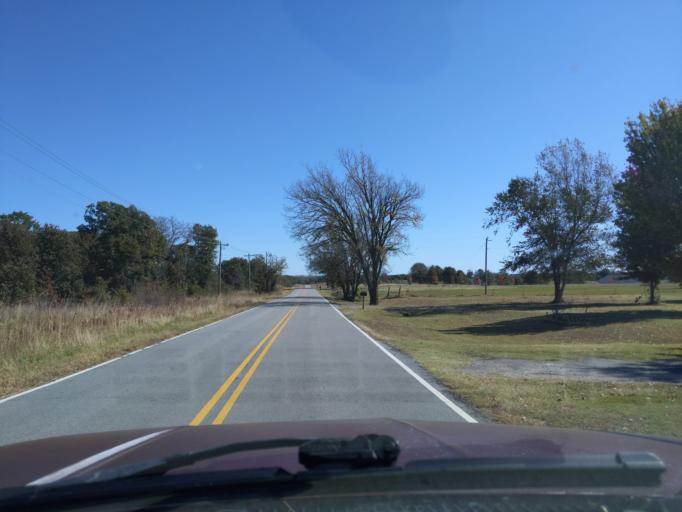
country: US
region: Oklahoma
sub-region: Creek County
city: Bristow
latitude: 35.7120
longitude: -96.3981
